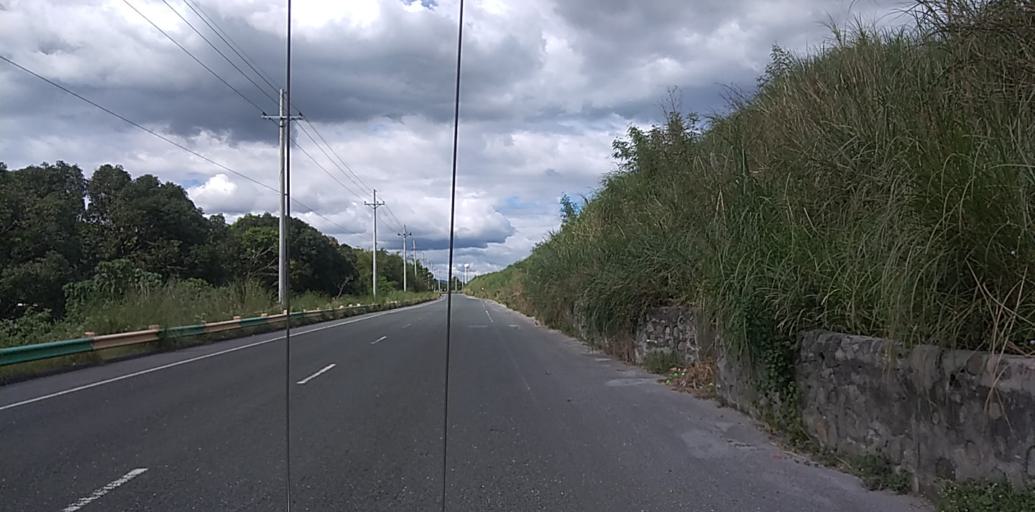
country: PH
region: Central Luzon
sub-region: Province of Pampanga
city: Dolores
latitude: 15.1027
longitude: 120.5228
